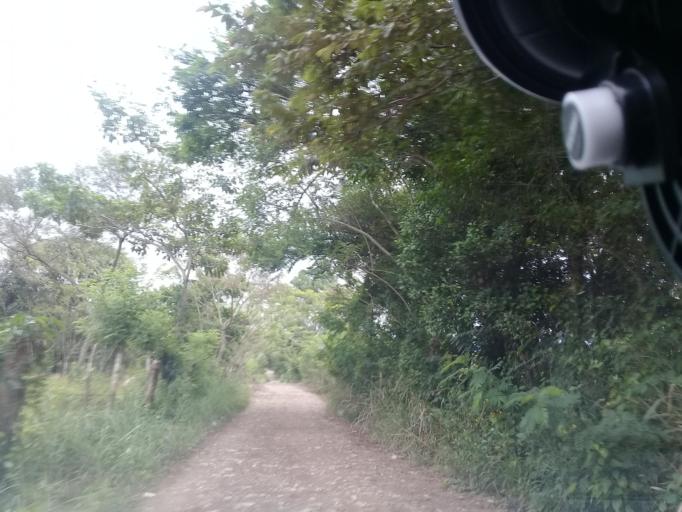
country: MX
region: Hidalgo
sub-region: Huejutla de Reyes
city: Parque de Poblamiento Solidaridad
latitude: 21.1749
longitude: -98.3767
